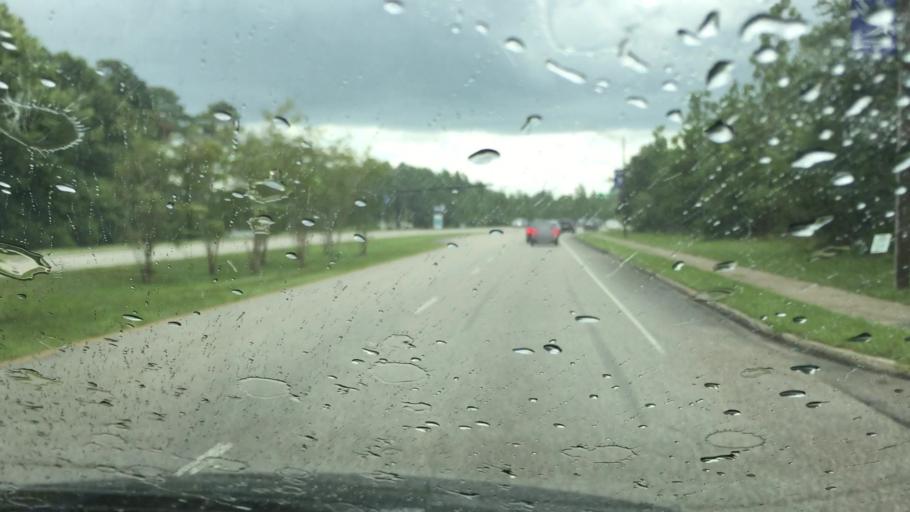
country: US
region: Florida
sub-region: Duval County
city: Jacksonville Beach
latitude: 30.2564
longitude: -81.4986
